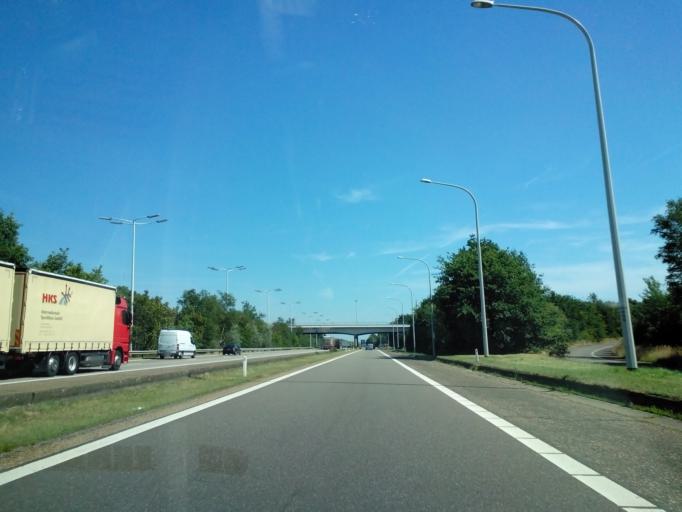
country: BE
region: Flanders
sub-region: Provincie Limburg
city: Genk
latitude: 50.9931
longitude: 5.4979
